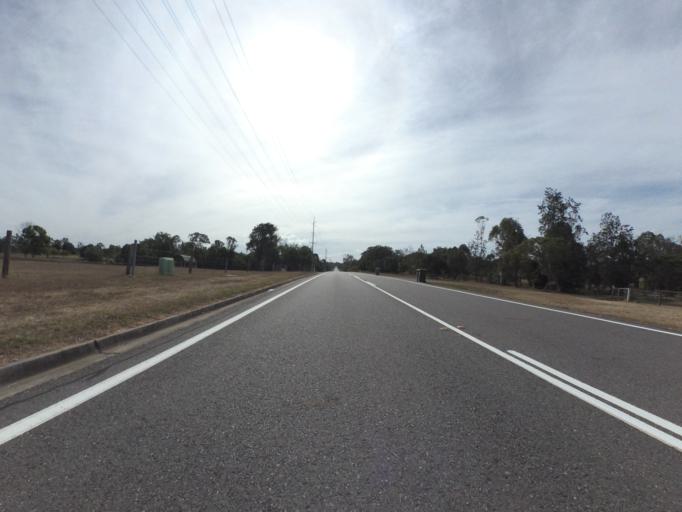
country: AU
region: Queensland
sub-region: Brisbane
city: Moggill
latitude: -27.5897
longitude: 152.8606
